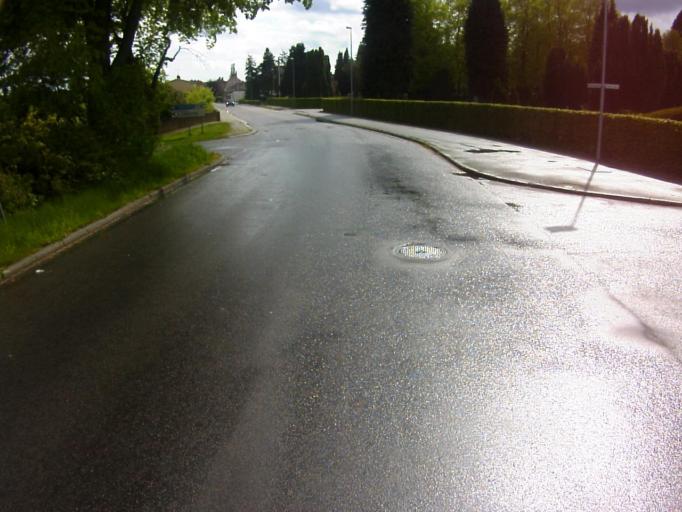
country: SE
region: Blekinge
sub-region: Solvesborgs Kommun
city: Soelvesborg
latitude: 56.0572
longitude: 14.5917
